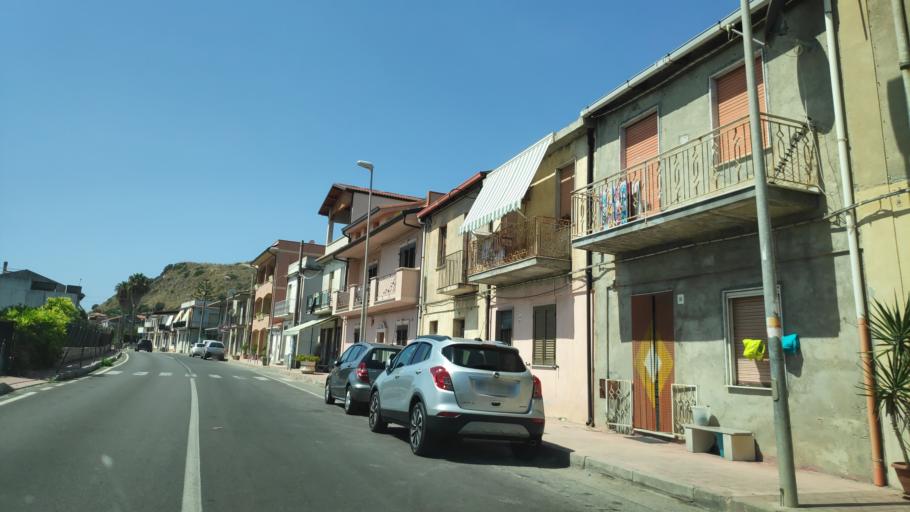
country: IT
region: Calabria
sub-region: Provincia di Reggio Calabria
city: Weather Station
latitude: 37.9321
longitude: 16.0685
